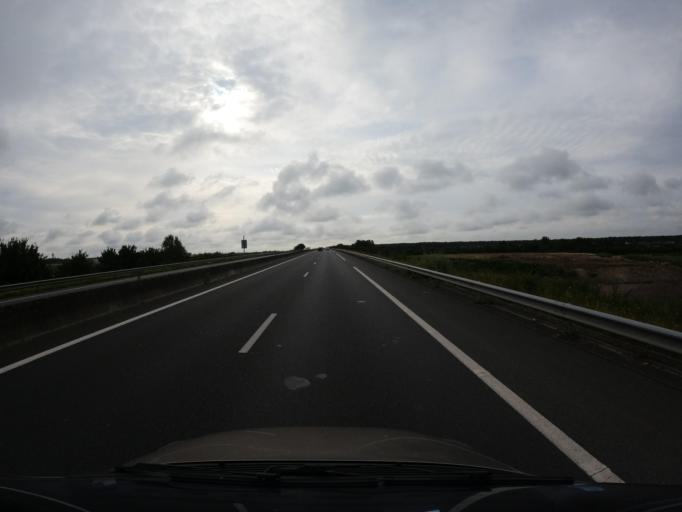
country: FR
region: Centre
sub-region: Departement d'Indre-et-Loire
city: Villandry
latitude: 47.3052
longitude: 0.5203
